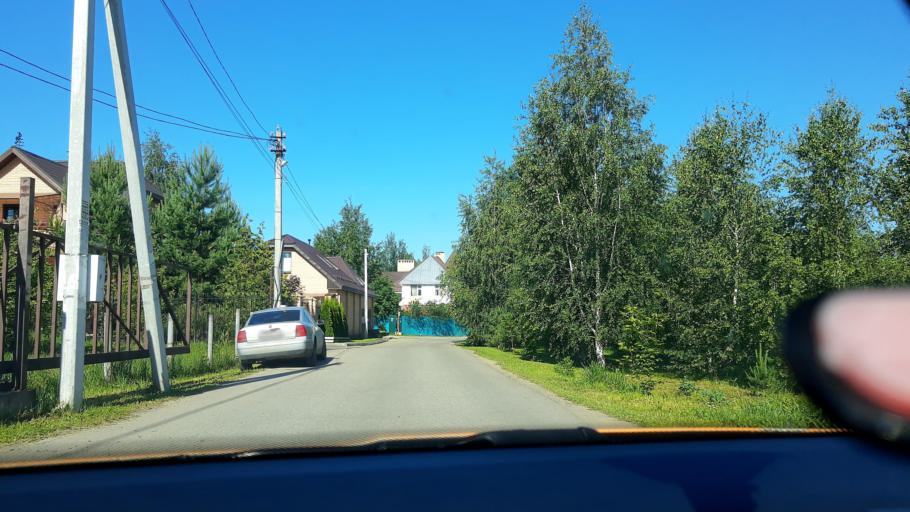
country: RU
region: Moskovskaya
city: Kommunarka
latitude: 55.5263
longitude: 37.4998
